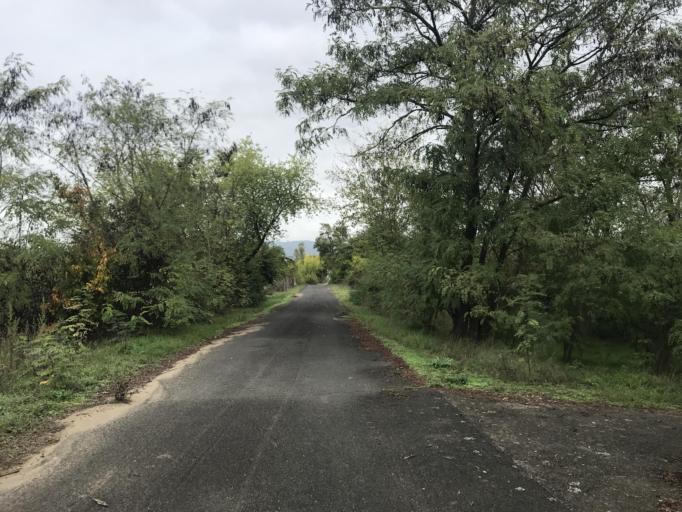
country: DE
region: Rheinland-Pfalz
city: Nieder-Ingelheim
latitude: 49.9857
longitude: 8.0636
